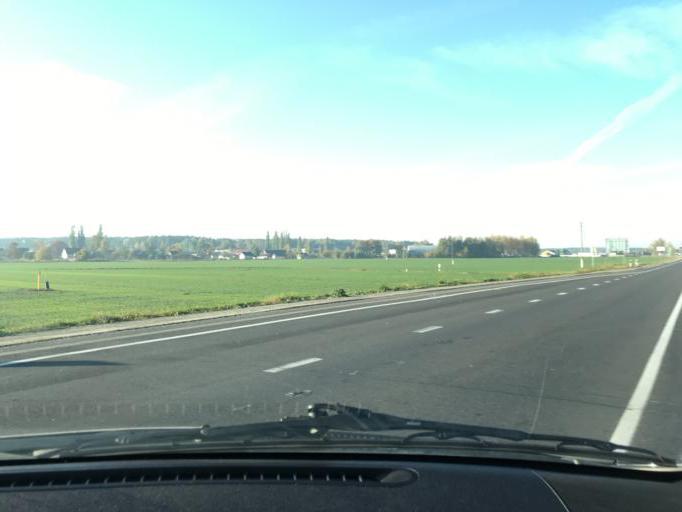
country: BY
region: Brest
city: Horad Pinsk
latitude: 52.1809
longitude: 26.0674
